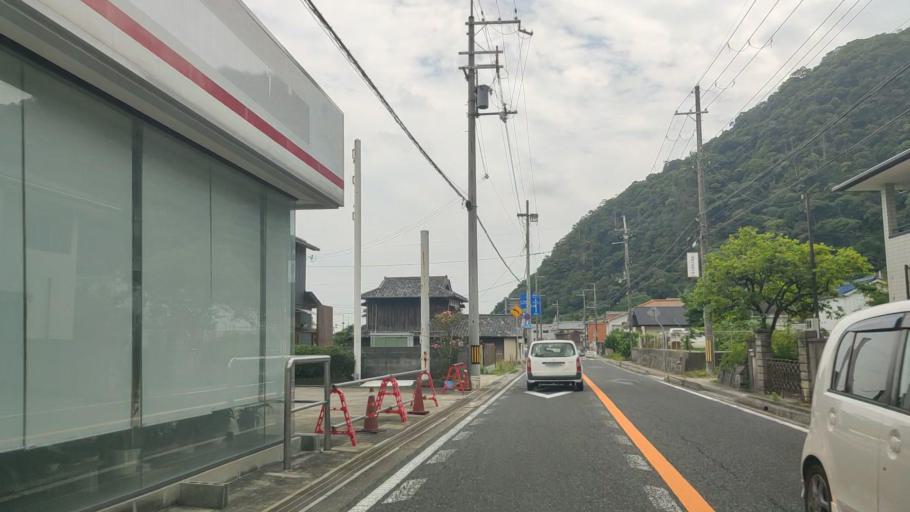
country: JP
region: Hyogo
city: Tatsunocho-tominaga
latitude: 34.8771
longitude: 134.5465
